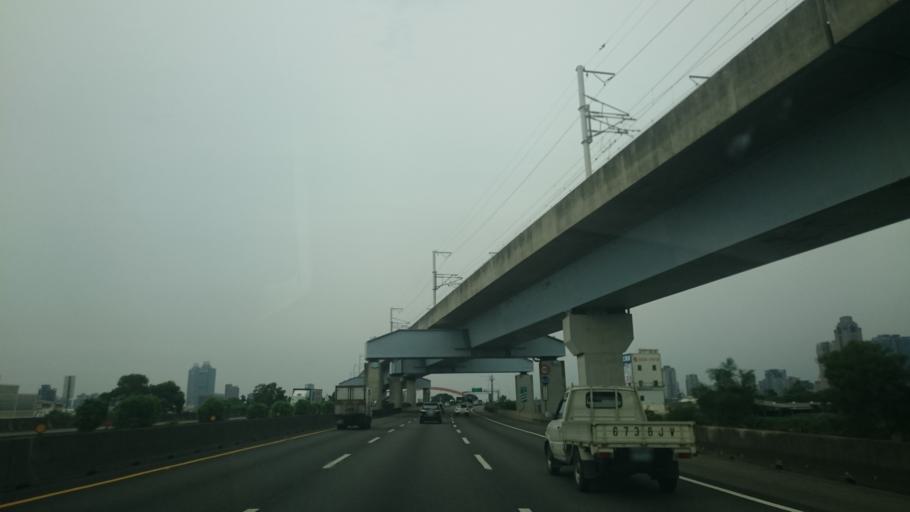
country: TW
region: Taiwan
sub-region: Taichung City
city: Taichung
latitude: 24.1642
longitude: 120.6223
